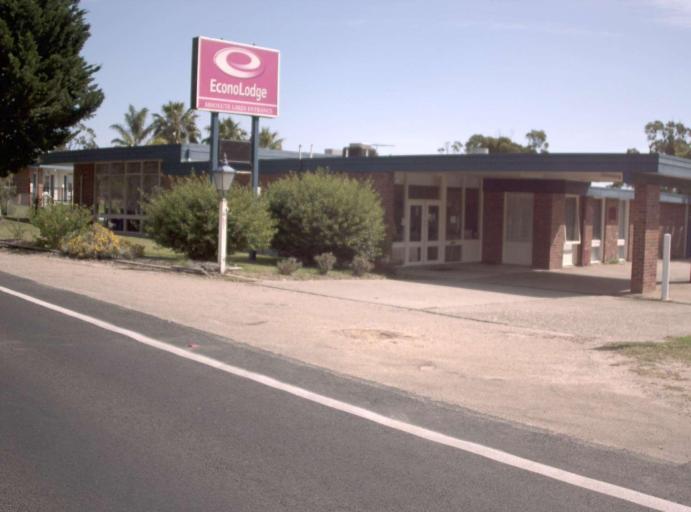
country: AU
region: Victoria
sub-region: East Gippsland
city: Lakes Entrance
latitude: -37.8783
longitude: 147.9612
